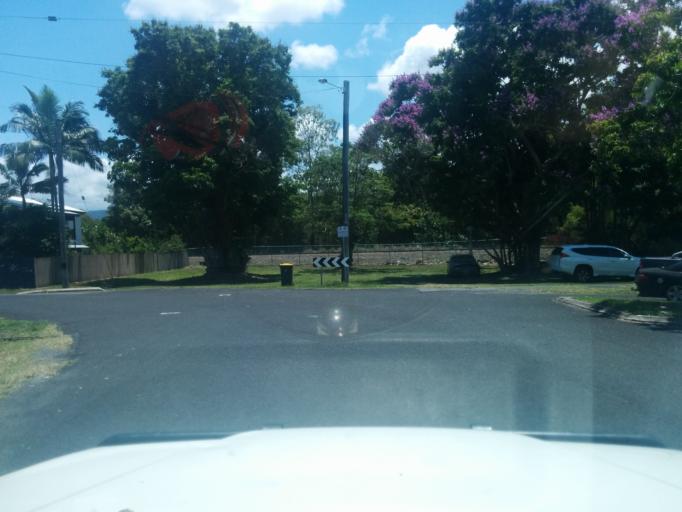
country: AU
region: Queensland
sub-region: Cairns
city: Cairns
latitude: -16.9057
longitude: 145.7567
